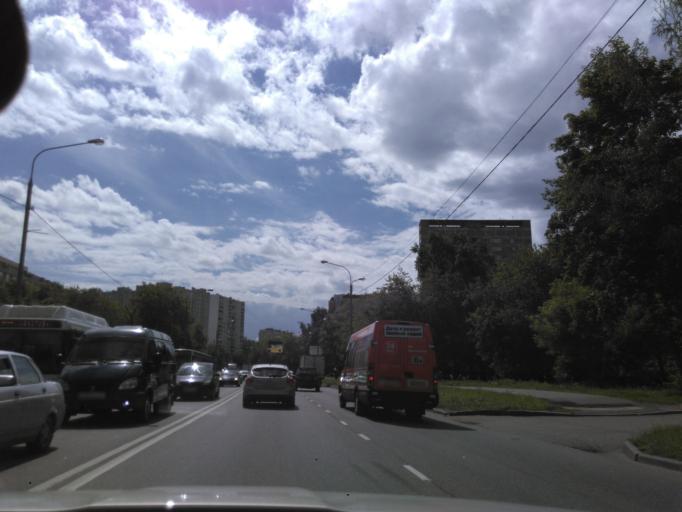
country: RU
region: Moscow
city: Golovinskiy
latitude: 55.8547
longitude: 37.5154
